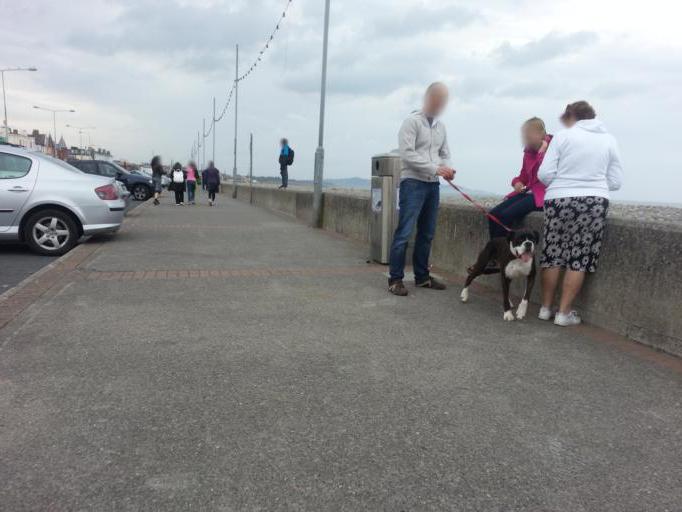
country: IE
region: Leinster
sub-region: Wicklow
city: Bray
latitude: 53.1969
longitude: -6.0931
